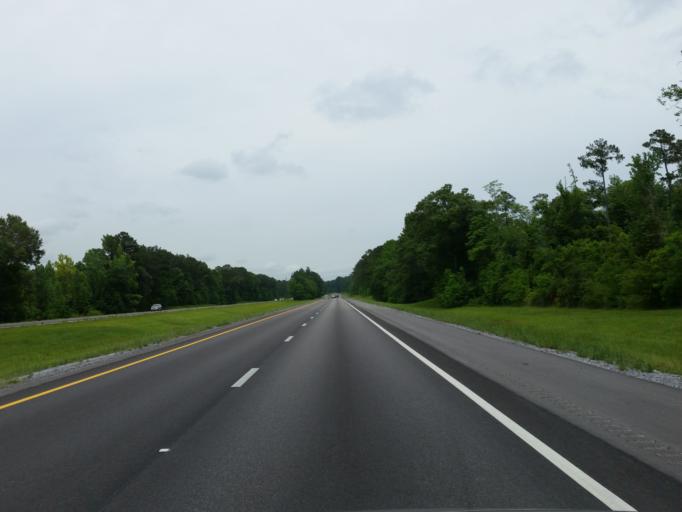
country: US
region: Mississippi
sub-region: Jones County
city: Sharon
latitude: 31.7536
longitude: -89.0712
